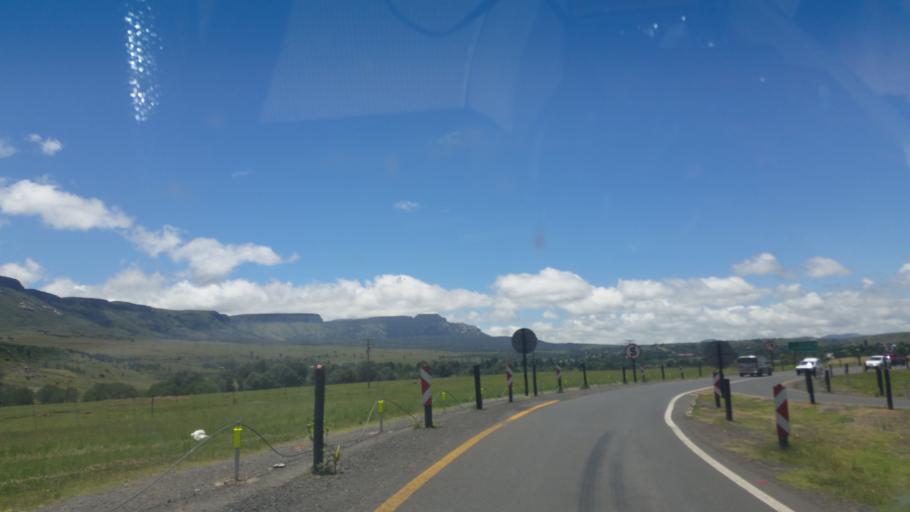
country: ZA
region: Orange Free State
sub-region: Thabo Mofutsanyana District Municipality
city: Harrismith
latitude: -28.2567
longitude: 29.1170
